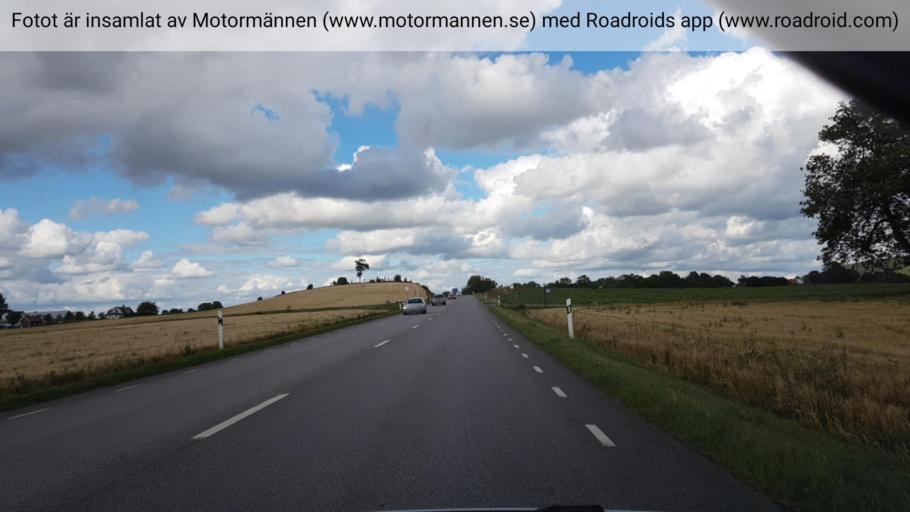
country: SE
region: Vaestra Goetaland
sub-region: Falkopings Kommun
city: Falkoeping
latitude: 58.1279
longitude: 13.5550
